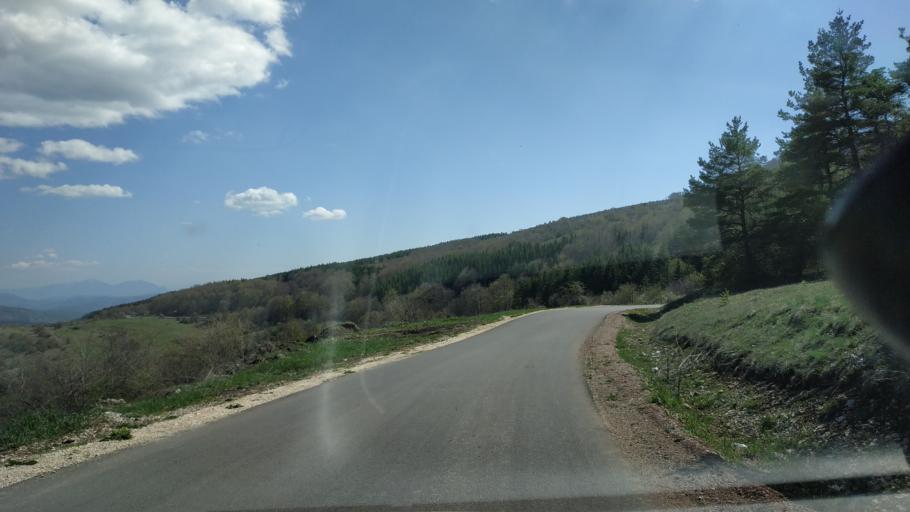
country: RS
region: Central Serbia
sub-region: Zajecarski Okrug
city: Soko Banja
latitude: 43.5898
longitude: 21.8881
